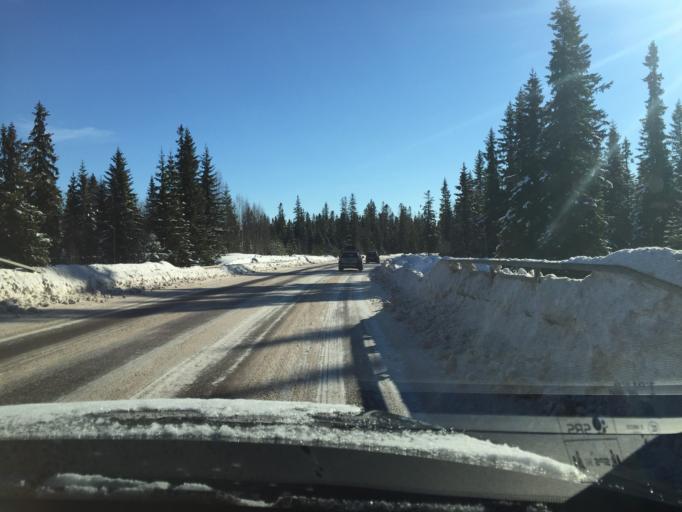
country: SE
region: Dalarna
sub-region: Malung-Saelens kommun
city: Malung
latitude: 61.1691
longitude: 13.1871
